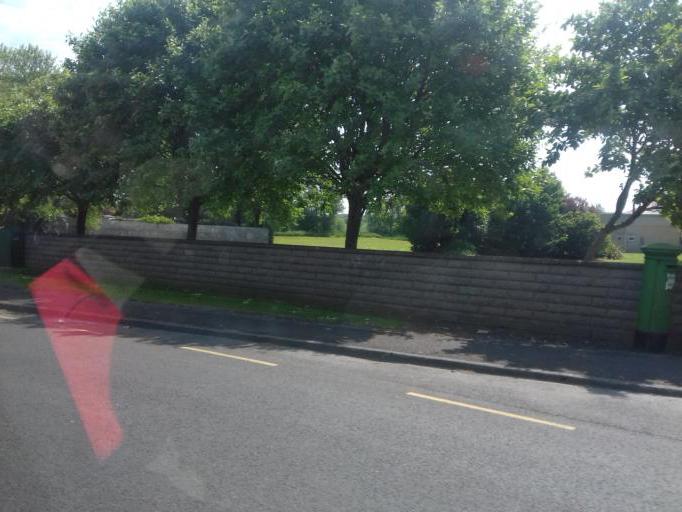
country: IE
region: Leinster
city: Portraine
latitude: 53.4932
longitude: -6.1143
